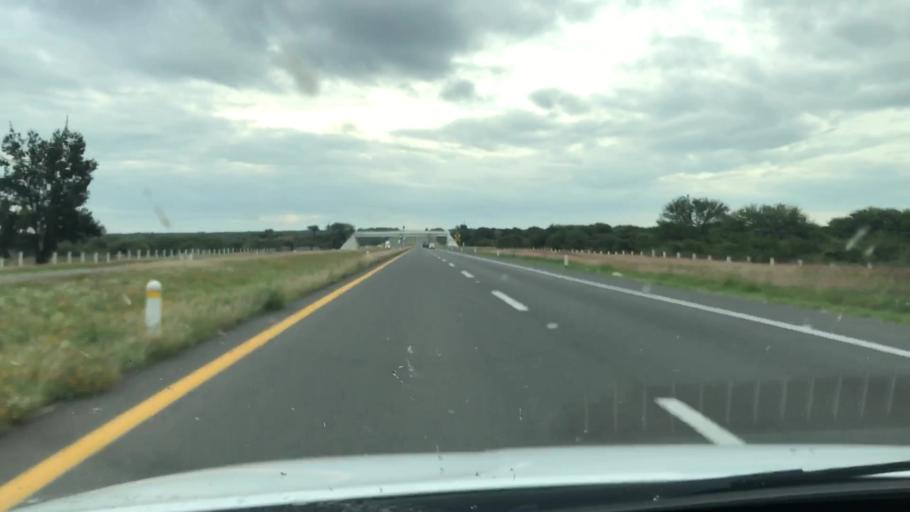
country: MX
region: Jalisco
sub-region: Lagos de Moreno
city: Cristeros [Fraccionamiento]
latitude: 21.2427
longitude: -101.9403
